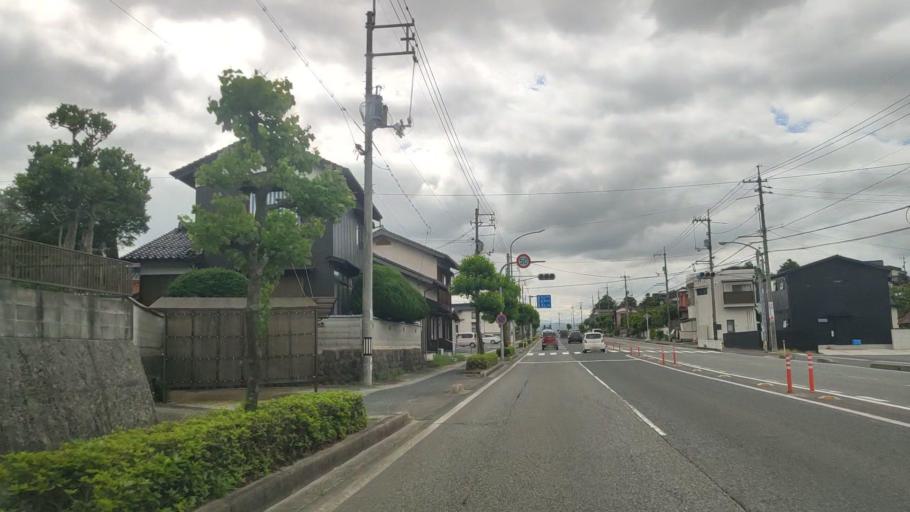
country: JP
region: Tottori
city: Yonago
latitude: 35.4038
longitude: 133.3690
